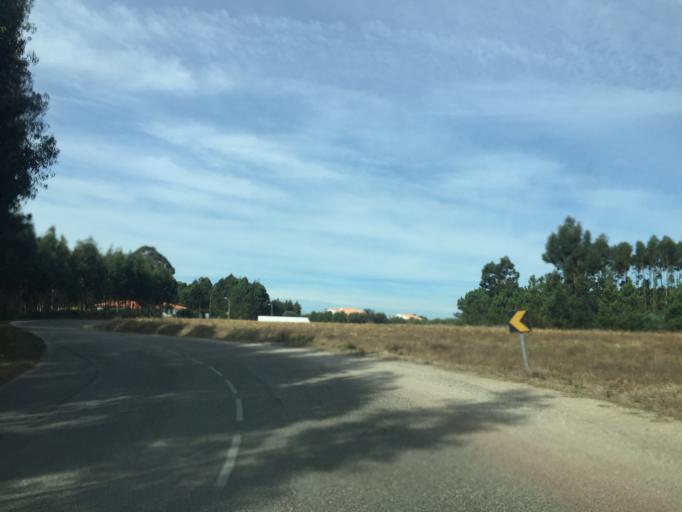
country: PT
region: Coimbra
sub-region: Figueira da Foz
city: Lavos
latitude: 40.0786
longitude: -8.8250
